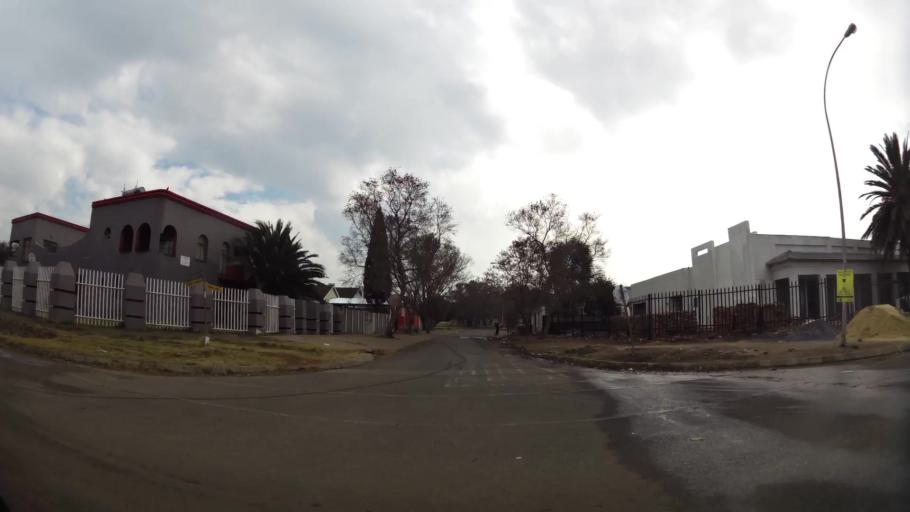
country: ZA
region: Gauteng
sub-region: Sedibeng District Municipality
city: Vanderbijlpark
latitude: -26.7125
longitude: 27.8604
